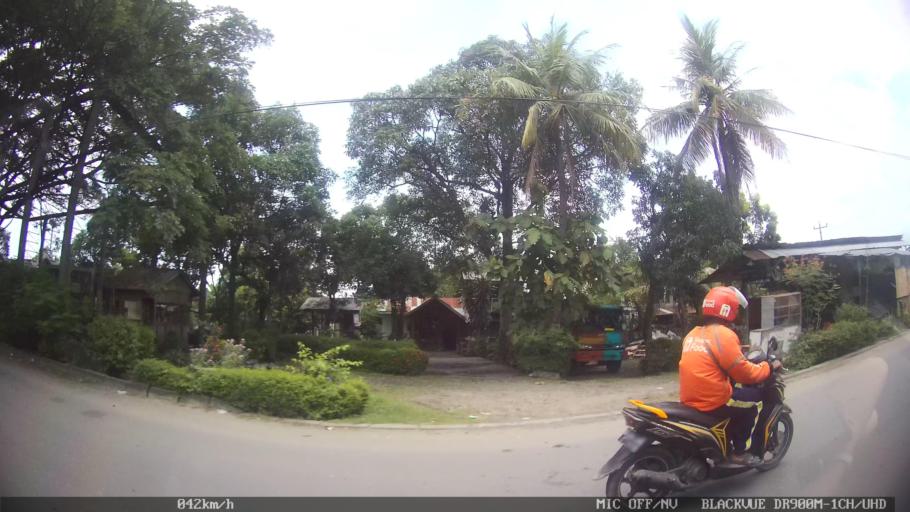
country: ID
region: North Sumatra
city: Labuhan Deli
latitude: 3.6915
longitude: 98.6710
